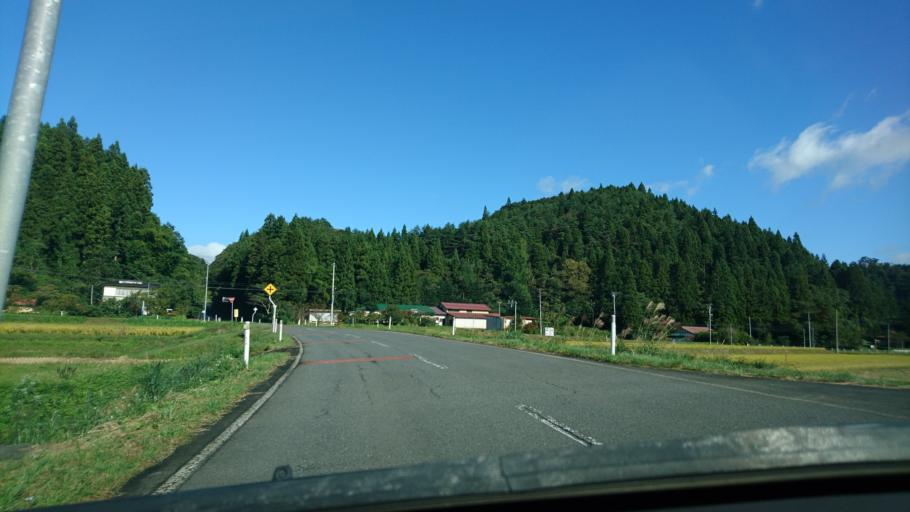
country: JP
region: Iwate
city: Ichinoseki
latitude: 39.0126
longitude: 141.0276
